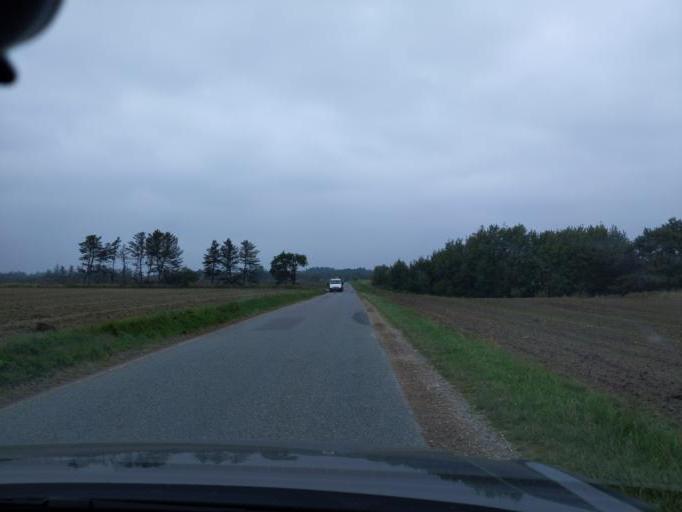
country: DK
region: Central Jutland
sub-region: Viborg Kommune
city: Stoholm
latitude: 56.4997
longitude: 9.2459
